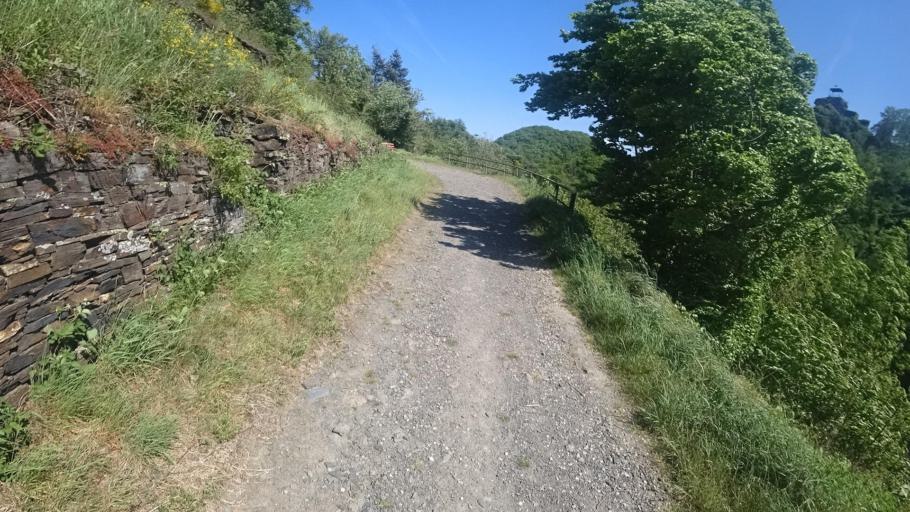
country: DE
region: Rheinland-Pfalz
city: Altenahr
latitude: 50.5193
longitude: 6.9936
